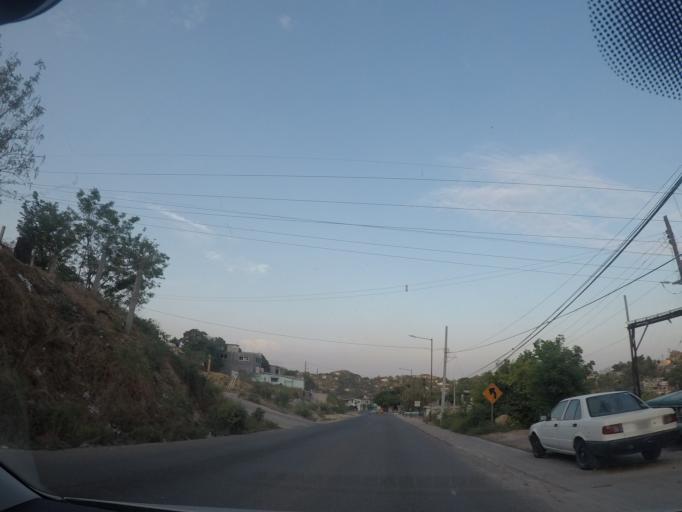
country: MX
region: Oaxaca
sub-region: Salina Cruz
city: Salina Cruz
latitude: 16.1929
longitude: -95.2084
